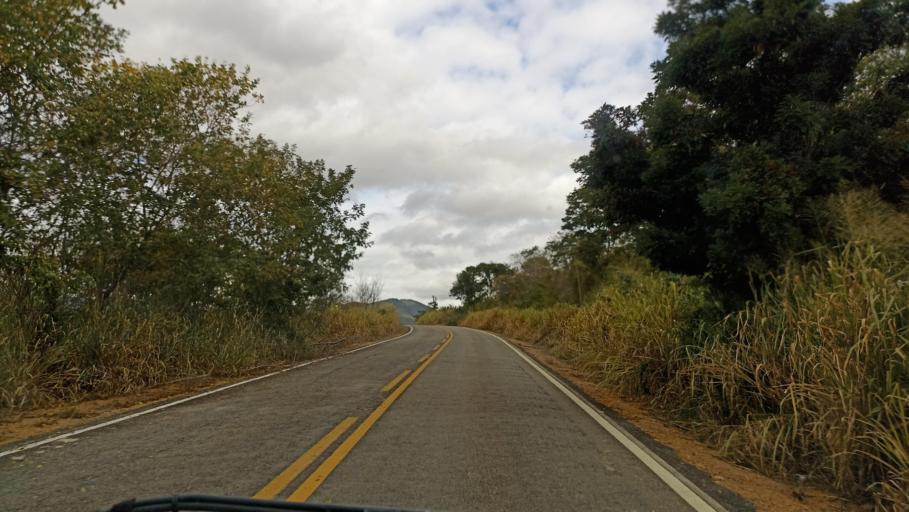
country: BR
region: Minas Gerais
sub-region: Joaima
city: Joaima
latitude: -16.6894
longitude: -40.9612
